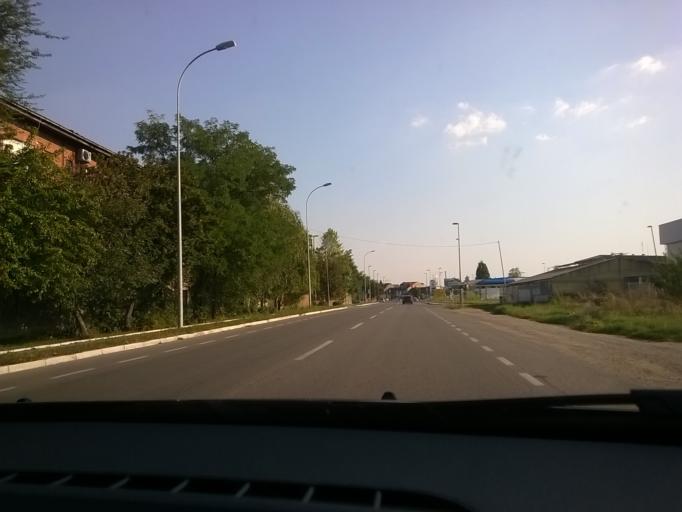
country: RS
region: Autonomna Pokrajina Vojvodina
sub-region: Juznobanatski Okrug
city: Vrsac
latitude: 45.1297
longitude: 21.2881
